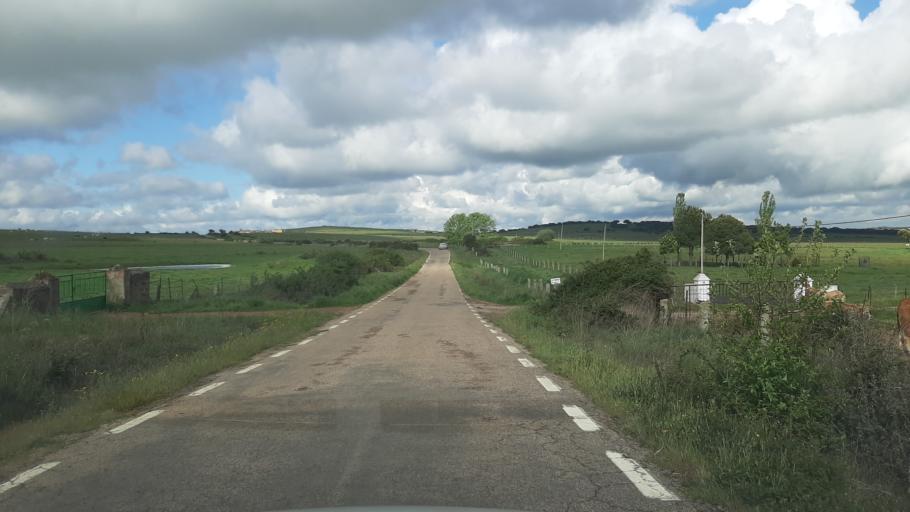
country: ES
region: Castille and Leon
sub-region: Provincia de Salamanca
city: Narros de Matalayegua
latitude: 40.7032
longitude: -5.9163
